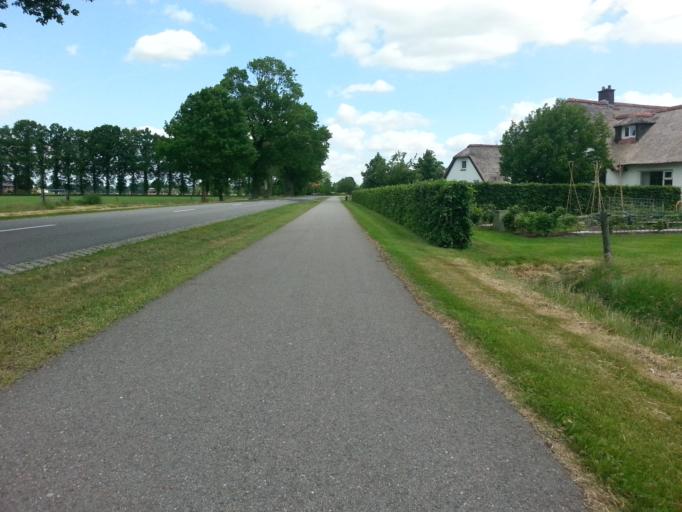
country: NL
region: Gelderland
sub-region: Gemeente Barneveld
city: Barneveld
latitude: 52.1054
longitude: 5.5489
